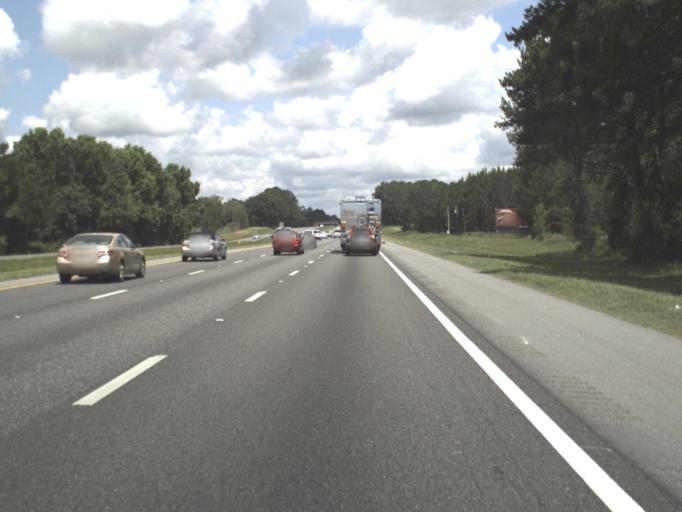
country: US
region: Florida
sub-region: Suwannee County
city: Wellborn
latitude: 30.2854
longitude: -82.7698
